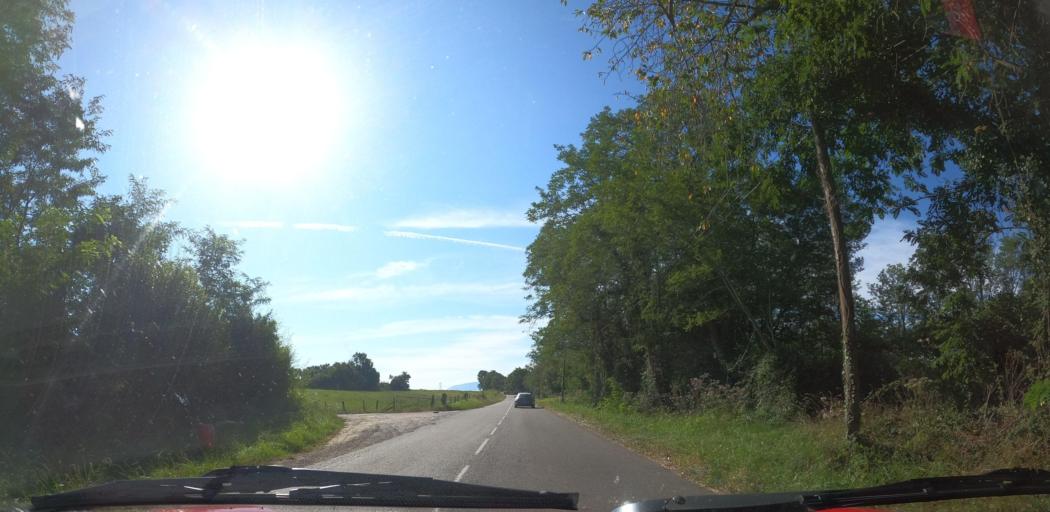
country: FR
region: Aquitaine
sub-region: Departement des Pyrenees-Atlantiques
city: Arcangues
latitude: 43.4002
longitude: -1.5339
